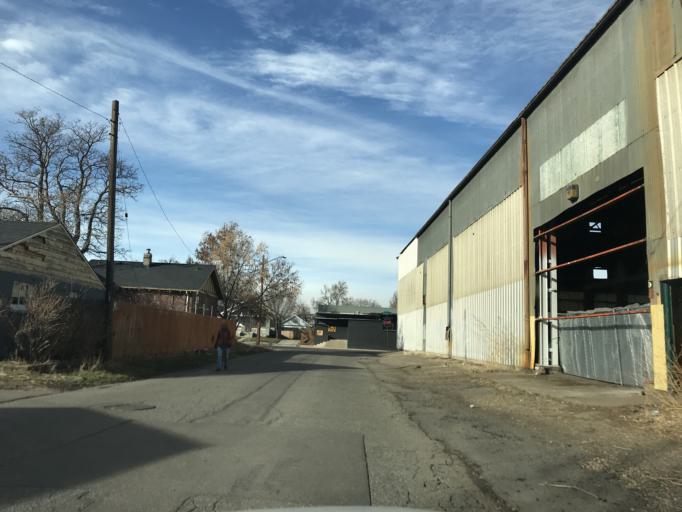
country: US
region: Colorado
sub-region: Denver County
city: Denver
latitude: 39.7693
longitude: -104.9627
